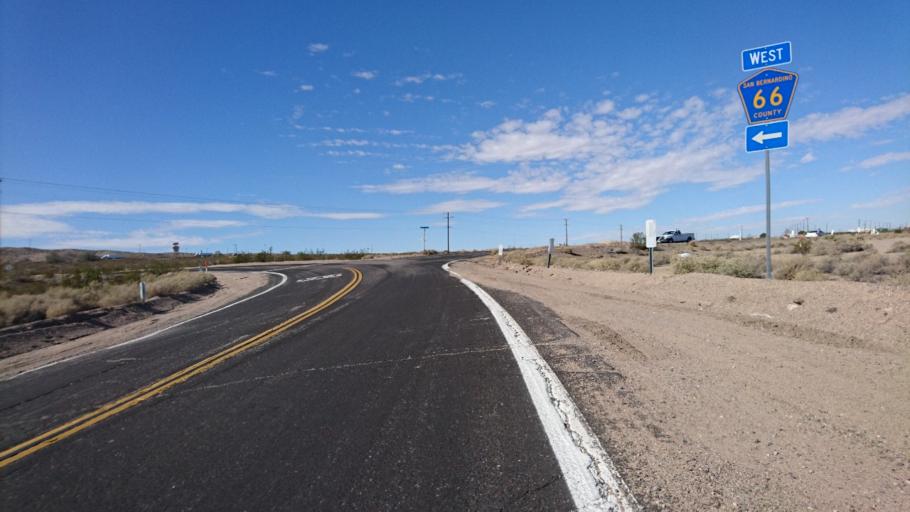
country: US
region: California
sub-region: San Bernardino County
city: Barstow
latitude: 34.8678
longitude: -116.9301
